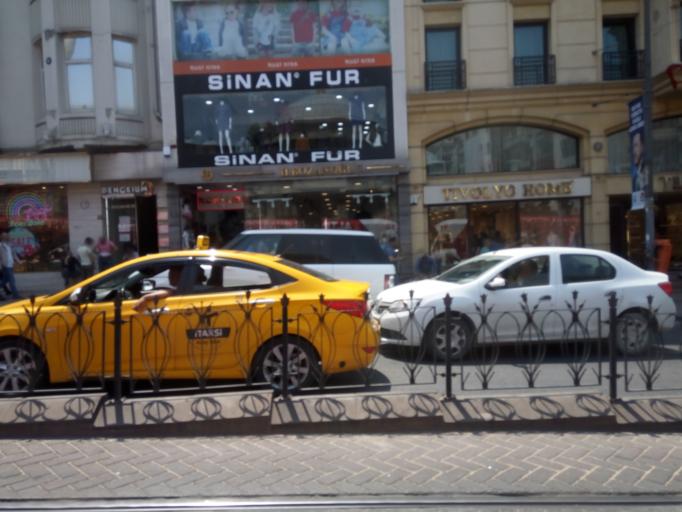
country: TR
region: Istanbul
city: Istanbul
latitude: 41.0097
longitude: 28.9564
